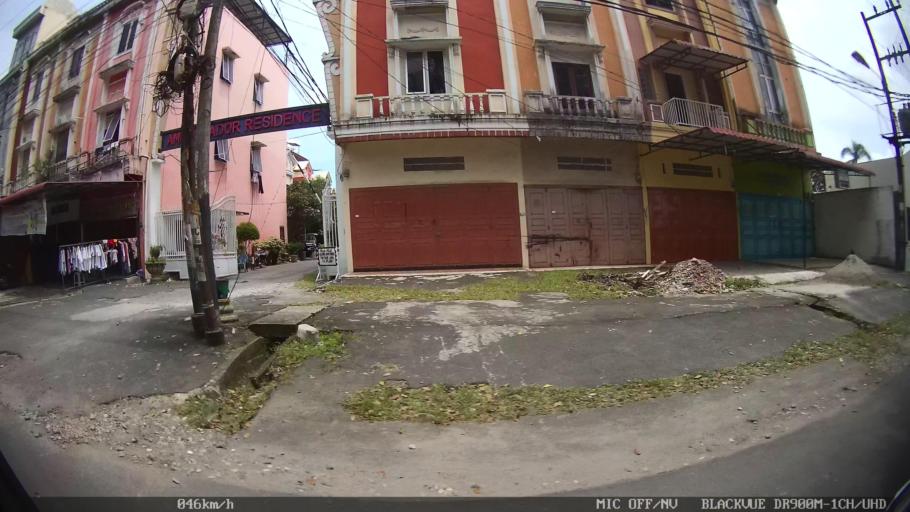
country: ID
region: North Sumatra
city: Sunggal
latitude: 3.5551
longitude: 98.6387
